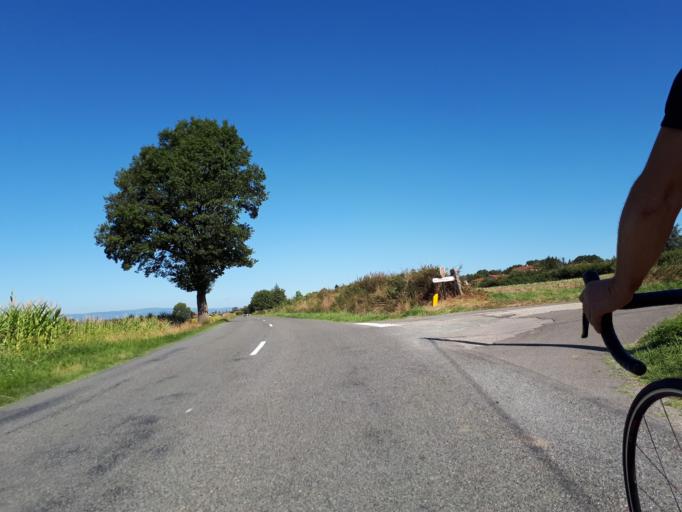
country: FR
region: Rhone-Alpes
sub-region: Departement de la Loire
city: Pouilly-les-Feurs
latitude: 45.7908
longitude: 4.2405
